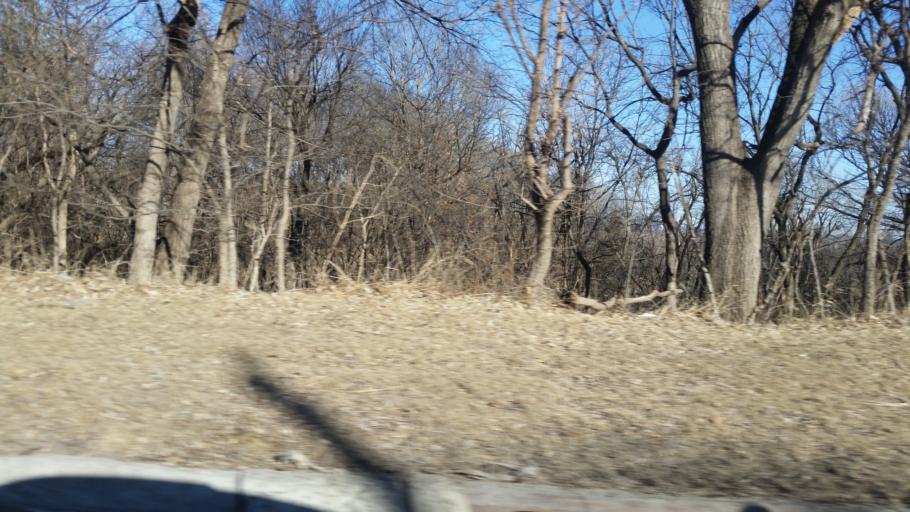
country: US
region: Nebraska
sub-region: Douglas County
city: Omaha
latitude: 41.1985
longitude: -95.9335
